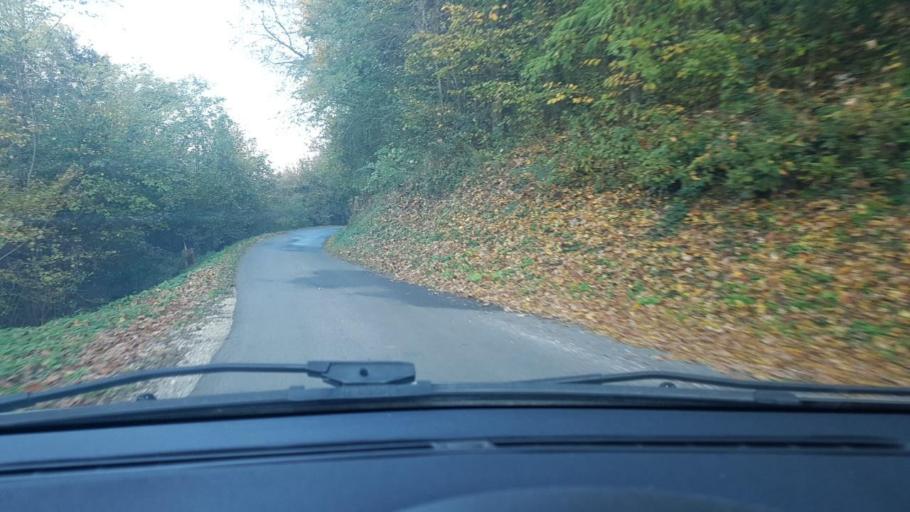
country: SI
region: Podcetrtek
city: Podcetrtek
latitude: 46.1500
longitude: 15.6062
